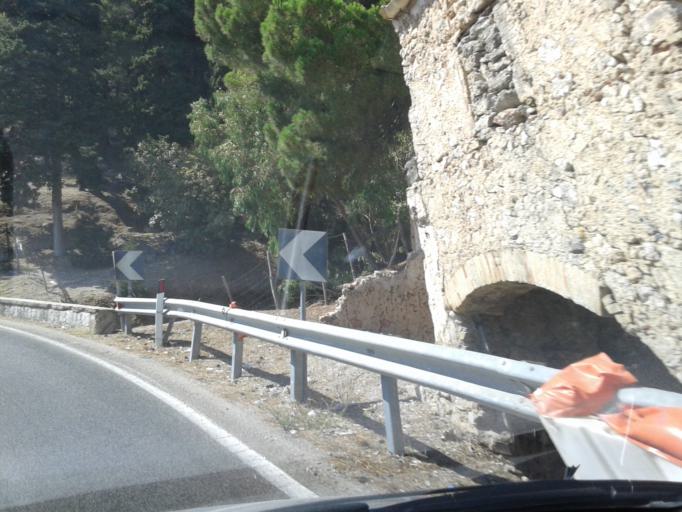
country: IT
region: Sicily
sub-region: Palermo
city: Pioppo
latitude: 38.0519
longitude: 13.2421
